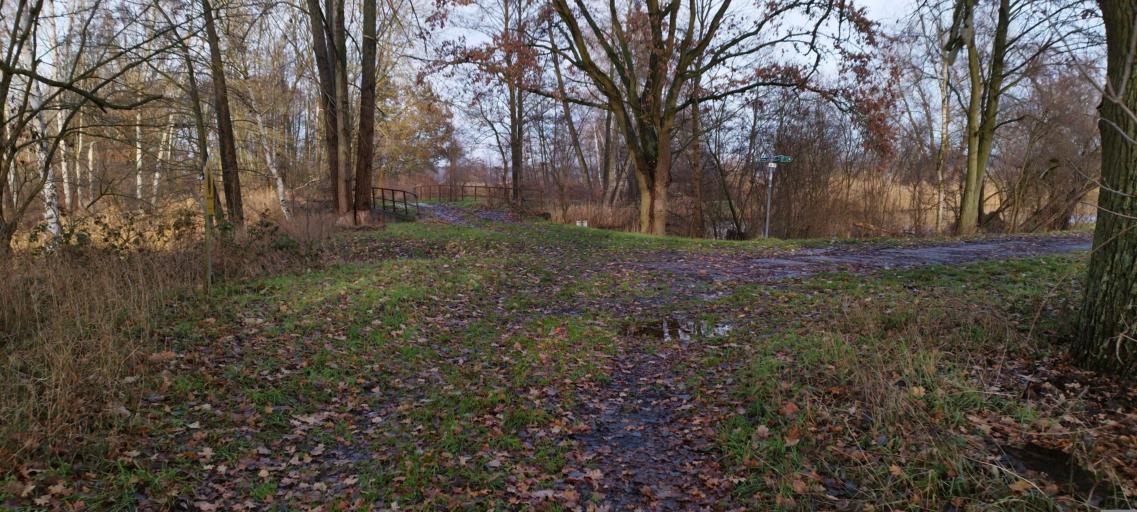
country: DE
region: Brandenburg
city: Munchehofe
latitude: 52.0818
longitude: 13.8354
